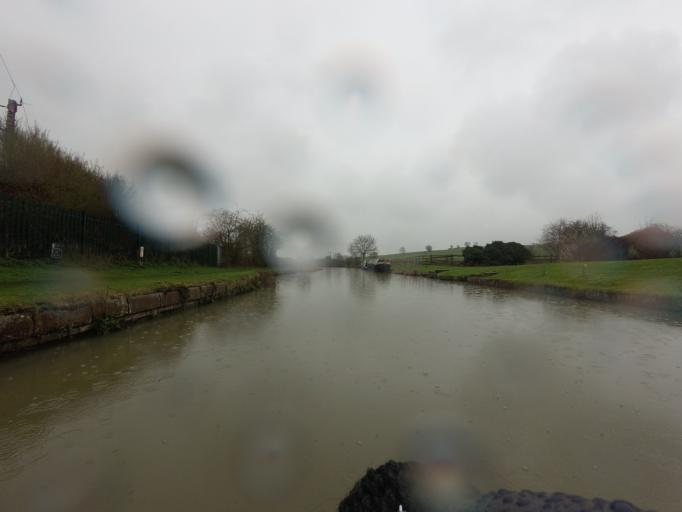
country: GB
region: England
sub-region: Northamptonshire
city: Blisworth
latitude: 52.1834
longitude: -0.9437
